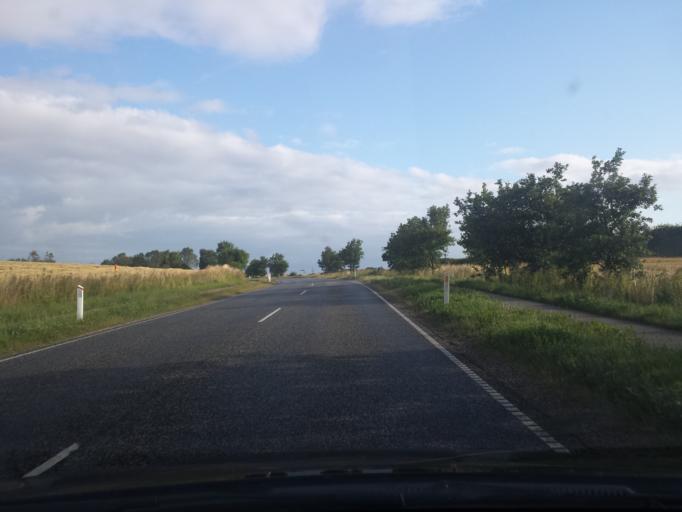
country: DK
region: South Denmark
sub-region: Sonderborg Kommune
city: Guderup
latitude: 55.0151
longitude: 9.8462
